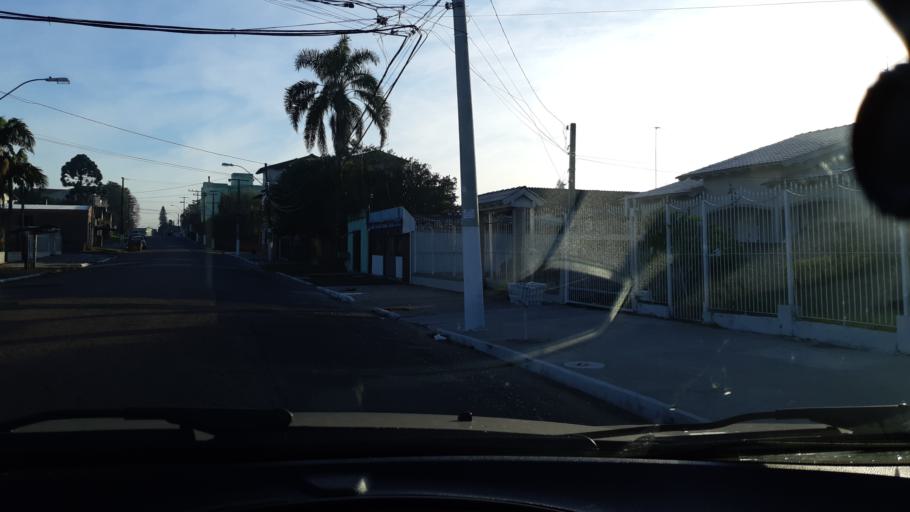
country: BR
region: Rio Grande do Sul
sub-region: Sapucaia Do Sul
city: Sapucaia
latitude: -29.8474
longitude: -51.1526
